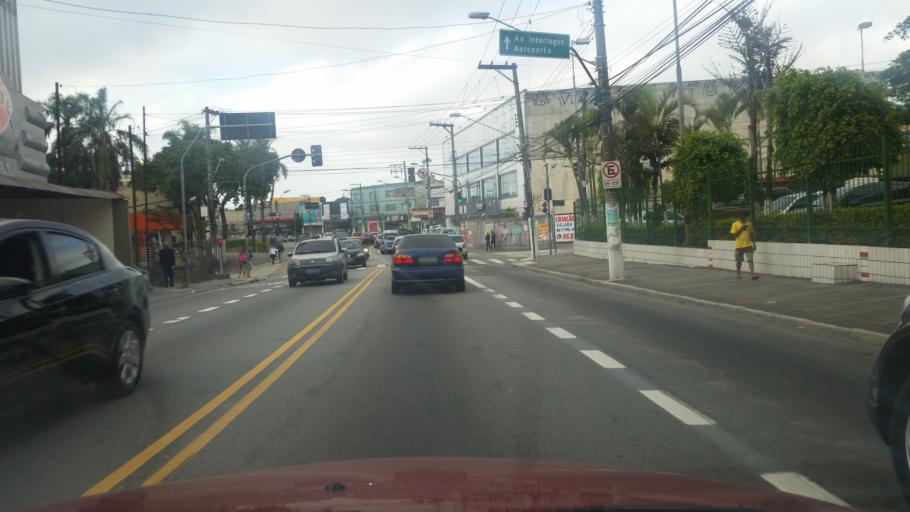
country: BR
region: Sao Paulo
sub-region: Diadema
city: Diadema
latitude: -23.7141
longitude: -46.6987
